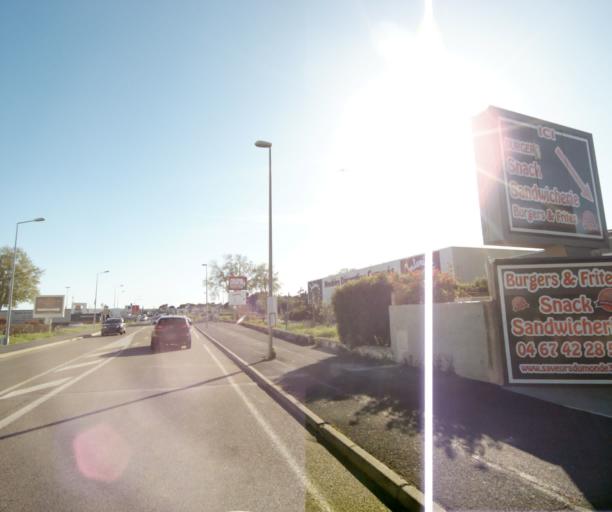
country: FR
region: Languedoc-Roussillon
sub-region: Departement de l'Herault
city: Lattes
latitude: 43.5850
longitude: 3.9274
